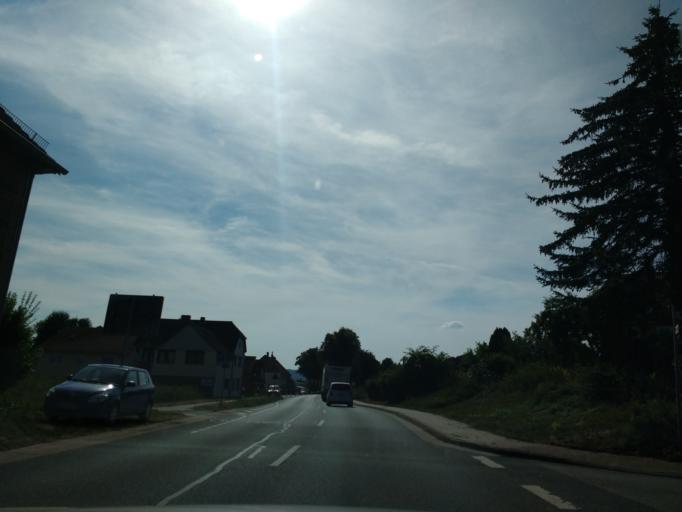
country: DE
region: Lower Saxony
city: Heinsen
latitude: 52.0929
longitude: 9.6469
